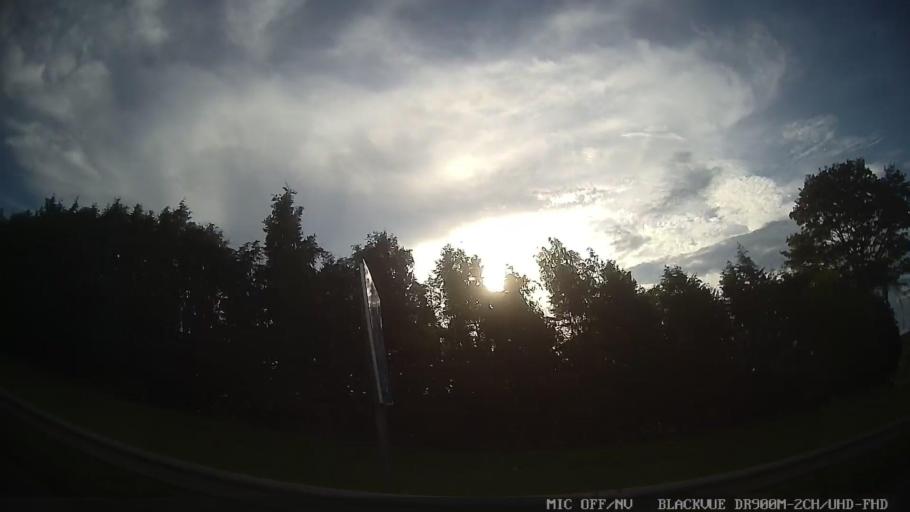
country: BR
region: Sao Paulo
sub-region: Tiete
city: Tiete
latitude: -23.1695
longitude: -47.6439
